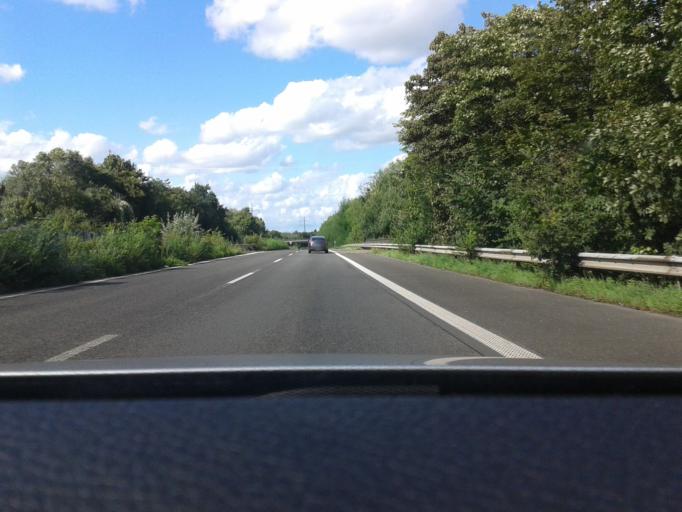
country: DE
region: North Rhine-Westphalia
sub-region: Regierungsbezirk Dusseldorf
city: Moers
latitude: 51.4221
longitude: 6.6807
